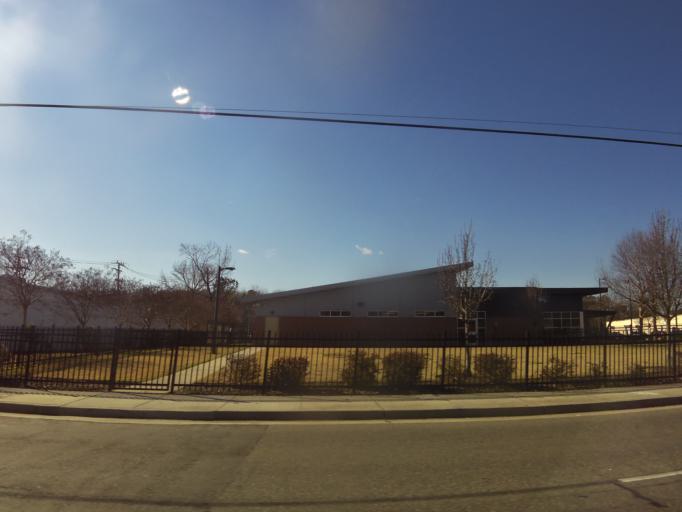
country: US
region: Virginia
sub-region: City of Newport News
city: Newport News
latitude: 37.0053
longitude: -76.4359
